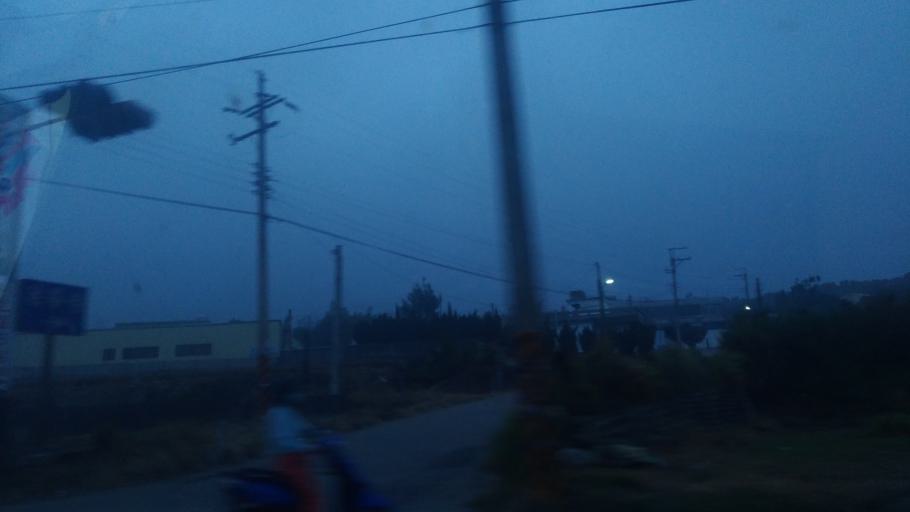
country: TW
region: Taiwan
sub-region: Miaoli
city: Miaoli
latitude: 24.5622
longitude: 120.7085
